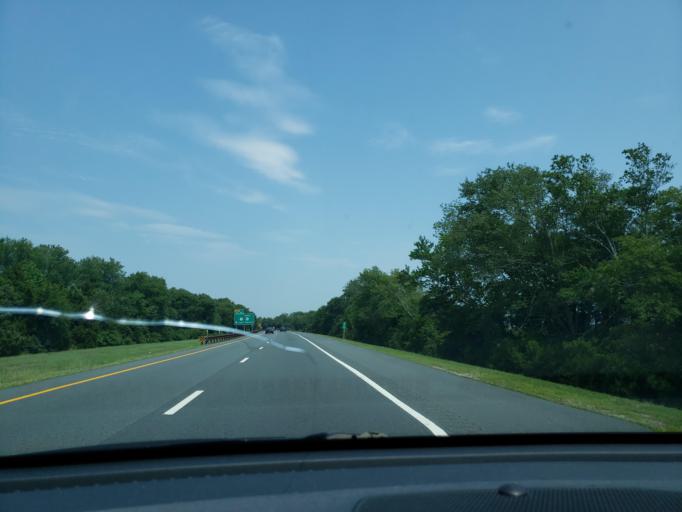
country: US
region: New Jersey
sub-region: Cape May County
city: Sea Isle City
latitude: 39.1999
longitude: -74.7024
